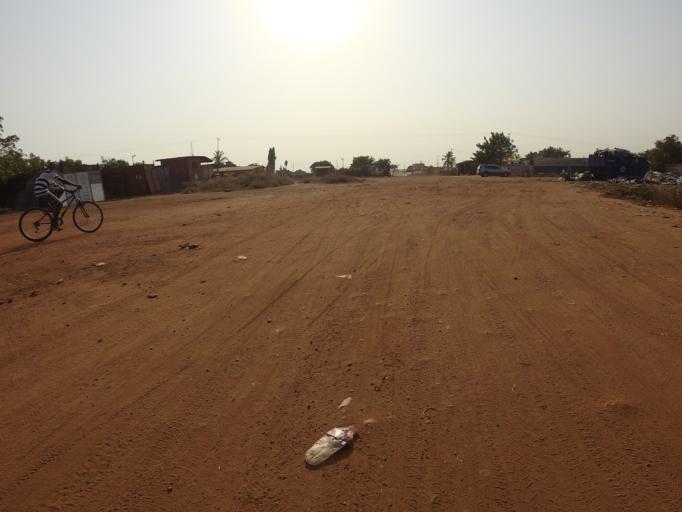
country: GH
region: Greater Accra
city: Tema
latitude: 5.7007
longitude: 0.0589
